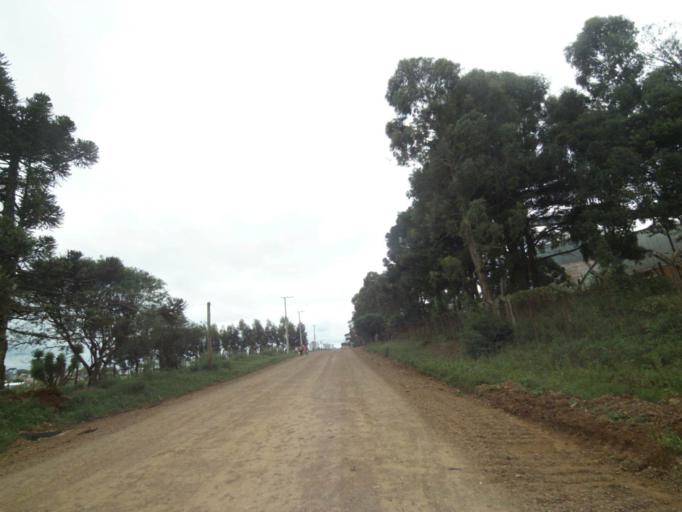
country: BR
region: Rio Grande do Sul
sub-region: Lagoa Vermelha
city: Lagoa Vermelha
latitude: -28.2111
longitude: -51.5084
